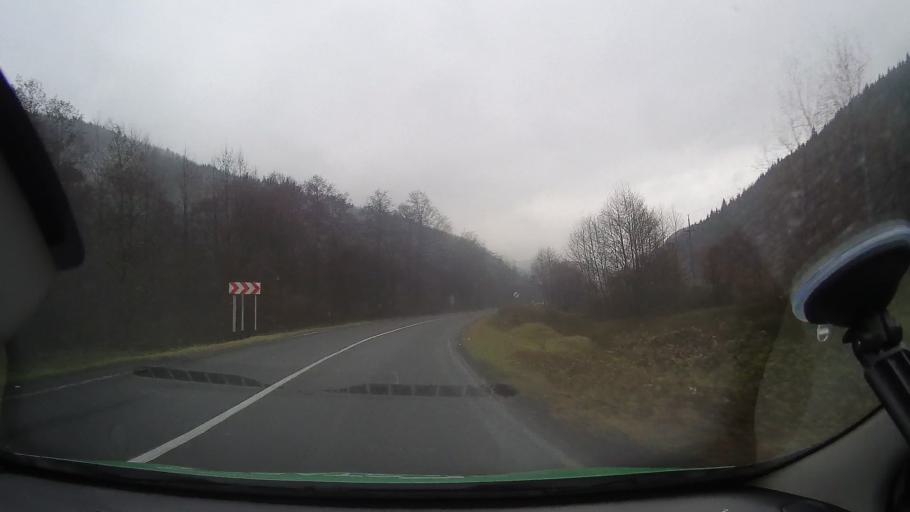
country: RO
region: Arad
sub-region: Comuna Plescuta
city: Plescuta
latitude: 46.3033
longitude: 22.4562
